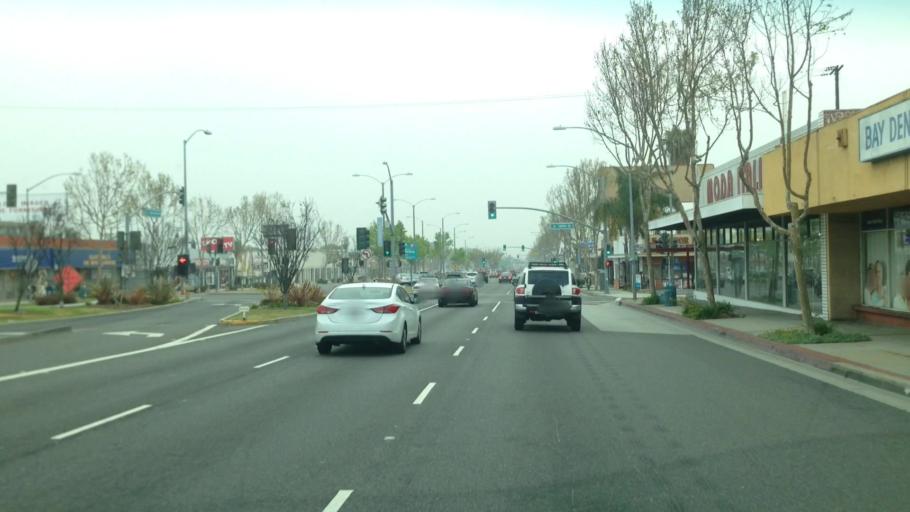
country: US
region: California
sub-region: Los Angeles County
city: Lawndale
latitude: 33.8769
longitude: -118.3524
